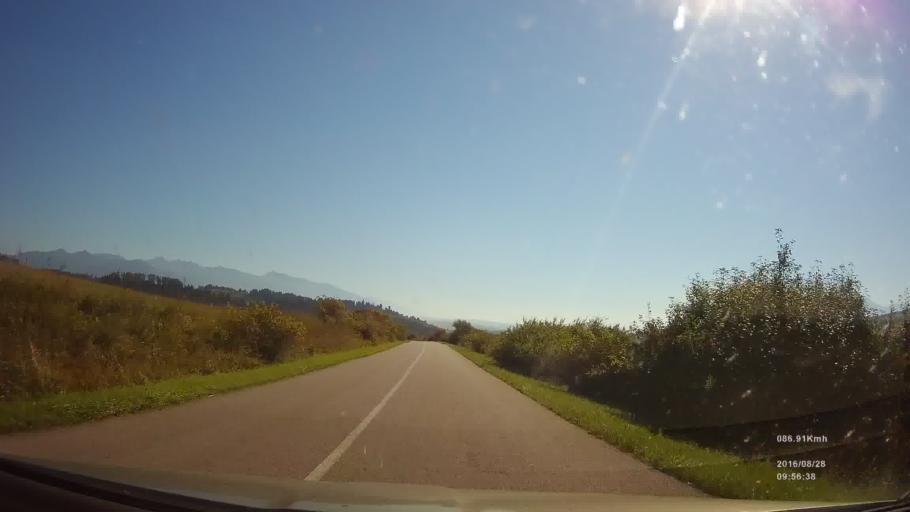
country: SK
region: Zilinsky
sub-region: Okres Liptovsky Mikulas
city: Liptovsky Mikulas
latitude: 49.1204
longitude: 19.4676
